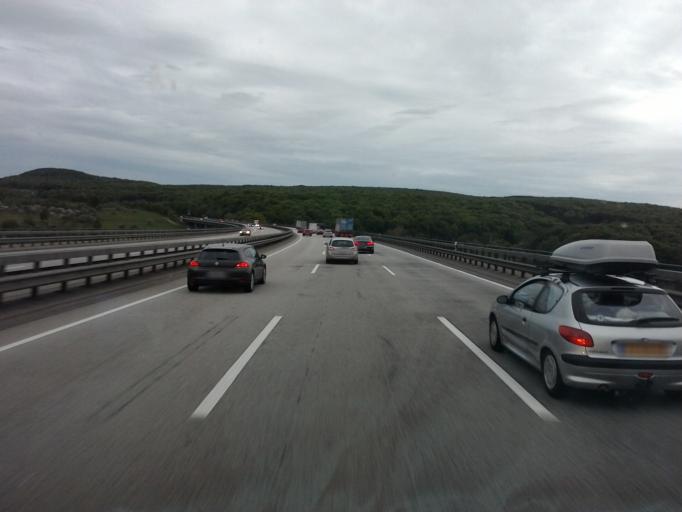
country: DE
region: Rheinland-Pfalz
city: Waldorf
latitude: 50.4892
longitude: 7.2196
